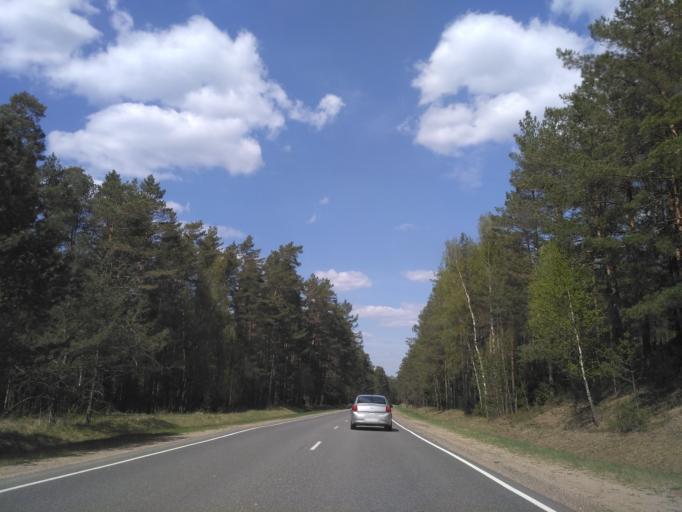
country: BY
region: Minsk
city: Myadzyel
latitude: 54.7970
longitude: 26.9419
